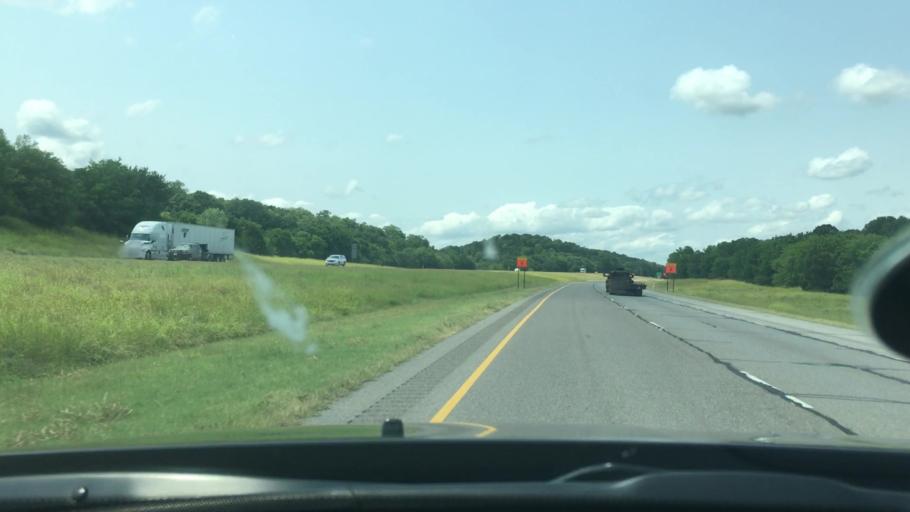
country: US
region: Oklahoma
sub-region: Murray County
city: Davis
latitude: 34.4684
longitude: -97.1520
